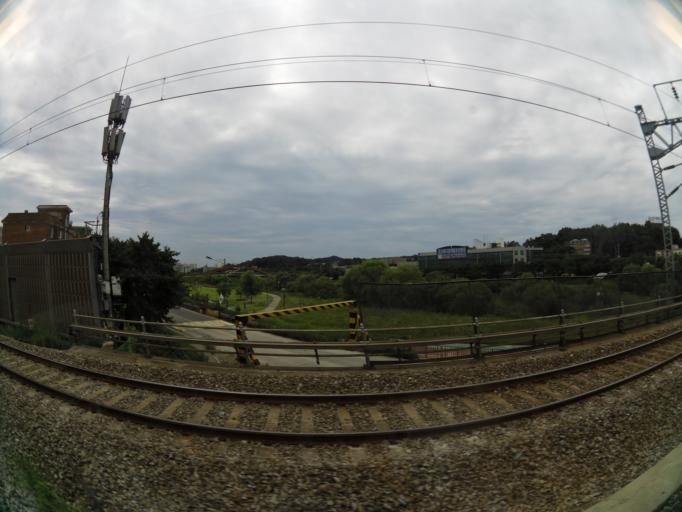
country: KR
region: Gyeonggi-do
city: Osan
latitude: 37.1535
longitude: 127.0670
